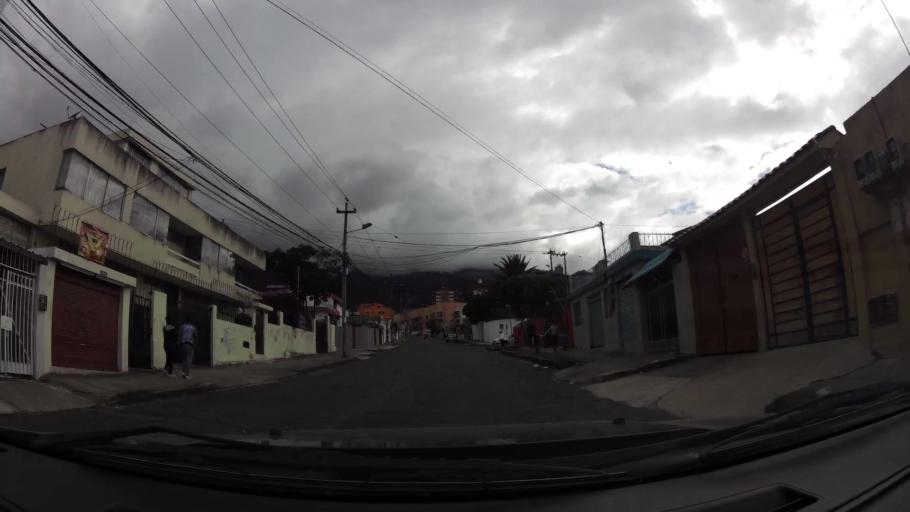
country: EC
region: Pichincha
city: Quito
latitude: -0.1396
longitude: -78.4982
